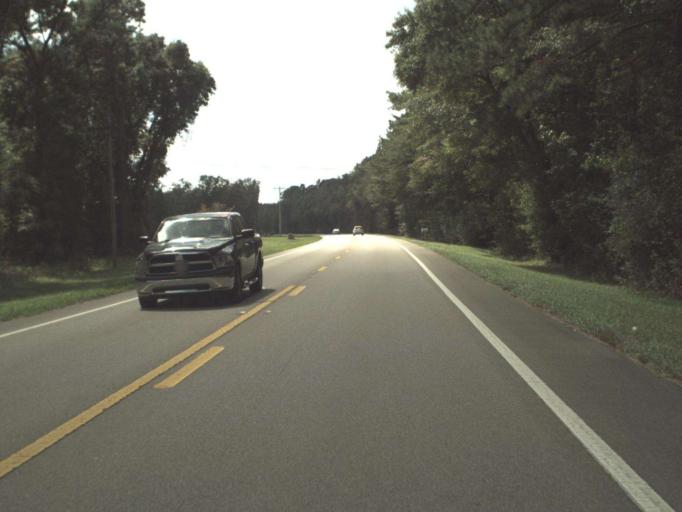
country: US
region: Florida
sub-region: Walton County
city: DeFuniak Springs
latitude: 30.6990
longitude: -85.9358
